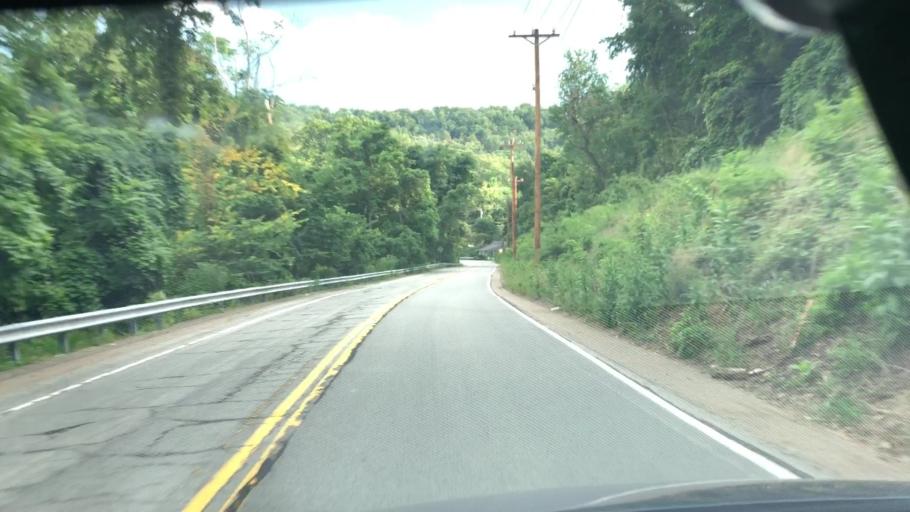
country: US
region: Pennsylvania
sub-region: Allegheny County
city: Blawnox
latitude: 40.4758
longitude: -79.8746
